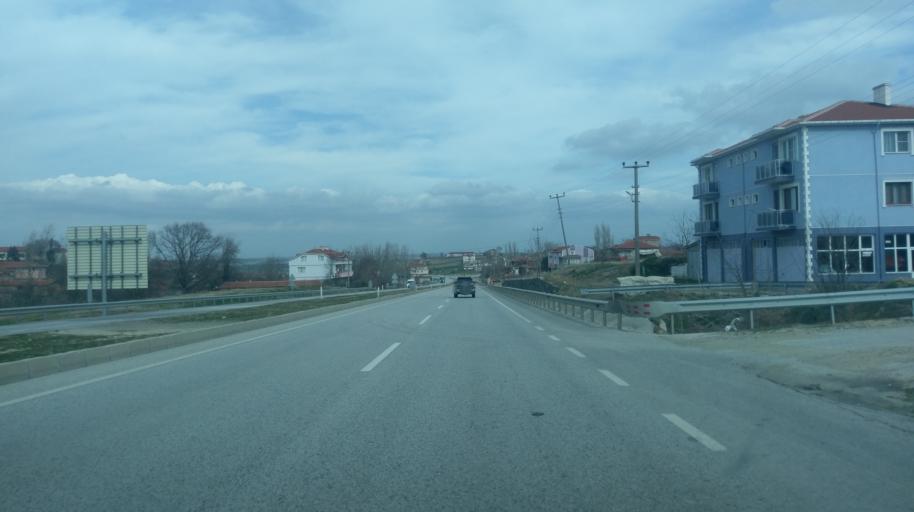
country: TR
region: Edirne
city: Kircasalih
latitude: 41.3928
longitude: 26.8036
